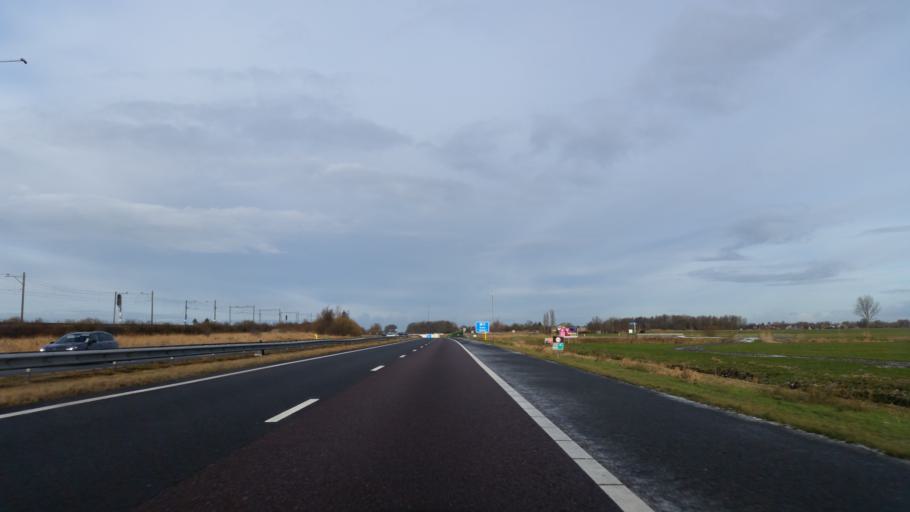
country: NL
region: Friesland
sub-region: Gemeente Boarnsterhim
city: Akkrum
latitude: 53.0727
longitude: 5.8320
